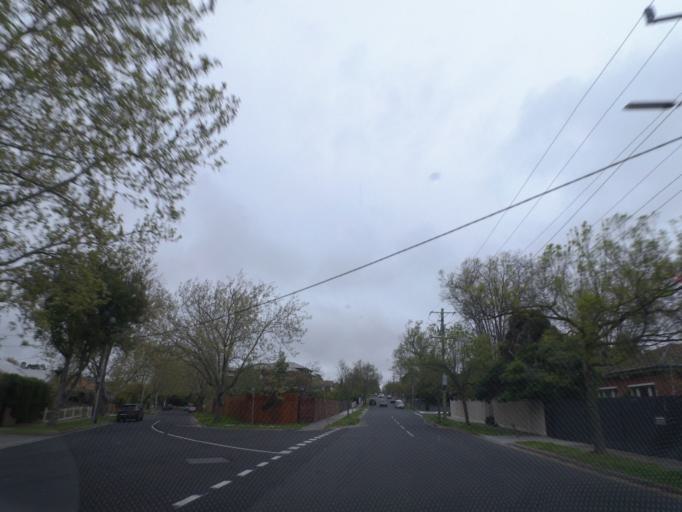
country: AU
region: Victoria
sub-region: Boroondara
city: Ashburton
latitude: -37.8653
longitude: 145.0670
